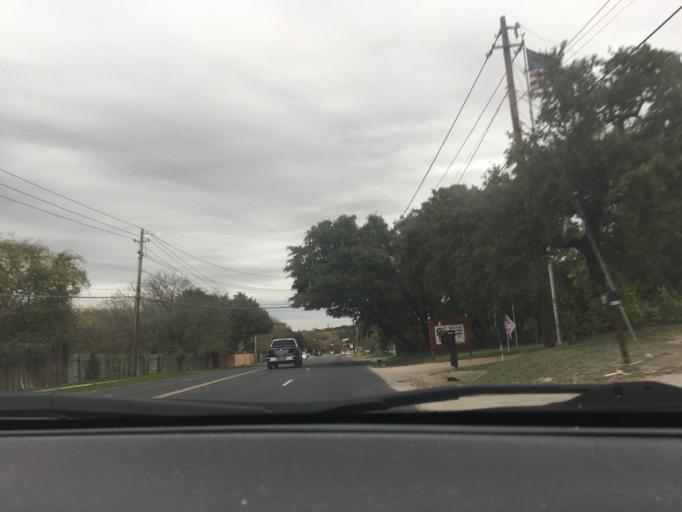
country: US
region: Texas
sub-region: Travis County
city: Onion Creek
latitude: 30.1779
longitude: -97.7970
